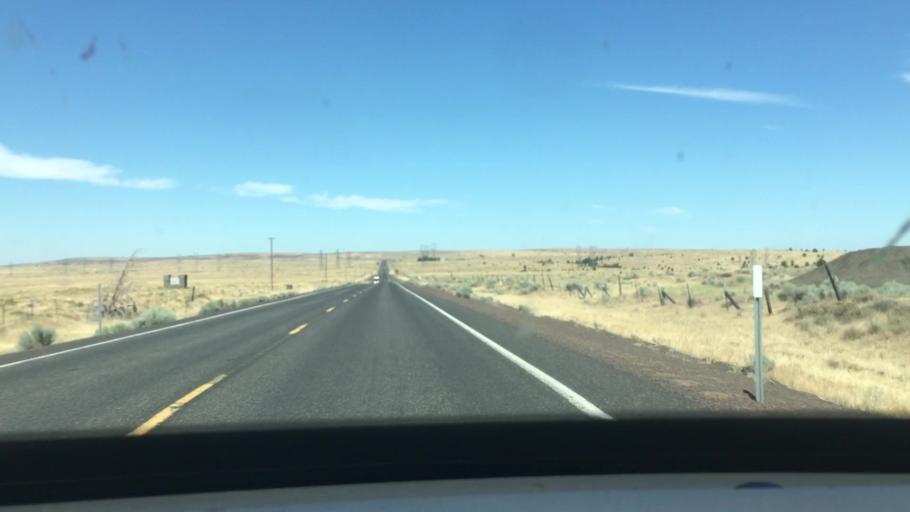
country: US
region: Oregon
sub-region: Jefferson County
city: Madras
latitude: 44.9450
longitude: -120.9160
